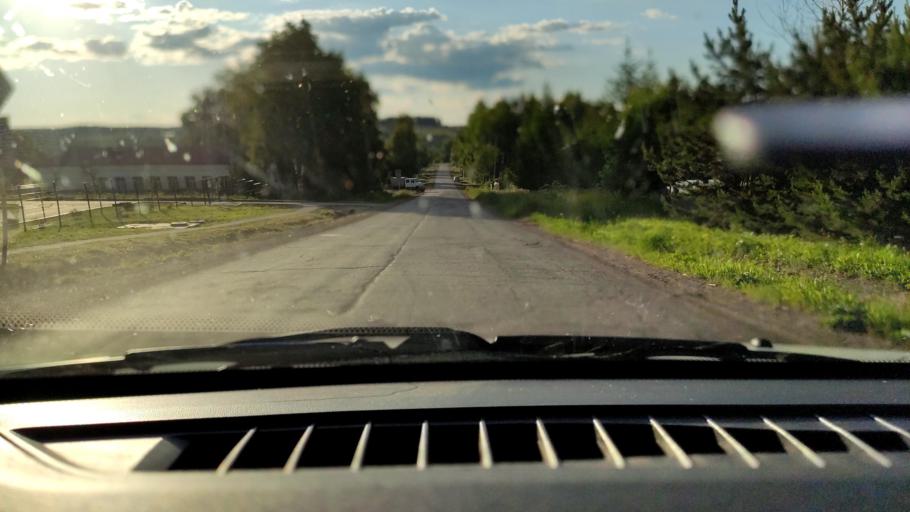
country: RU
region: Perm
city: Uinskoye
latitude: 57.1142
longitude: 56.5291
